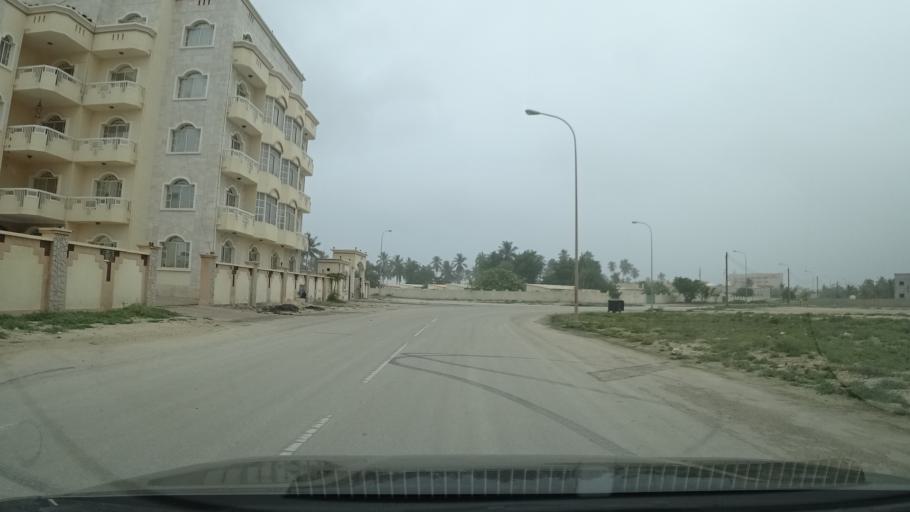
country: OM
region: Zufar
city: Salalah
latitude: 17.0103
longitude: 54.1557
